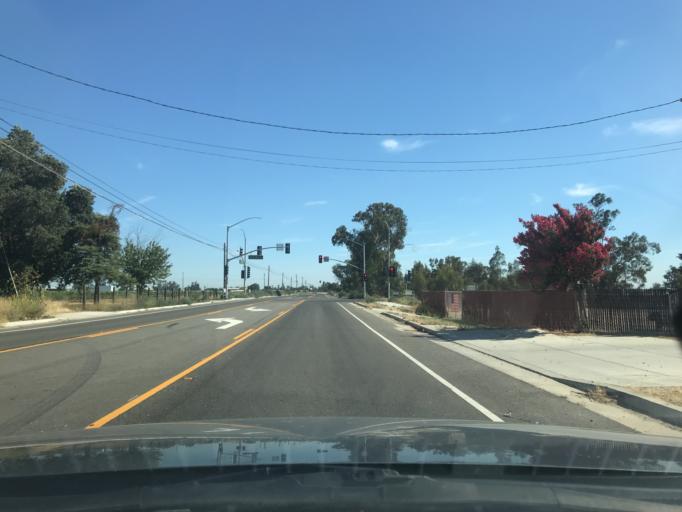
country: US
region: California
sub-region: Merced County
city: Atwater
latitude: 37.3395
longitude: -120.5588
